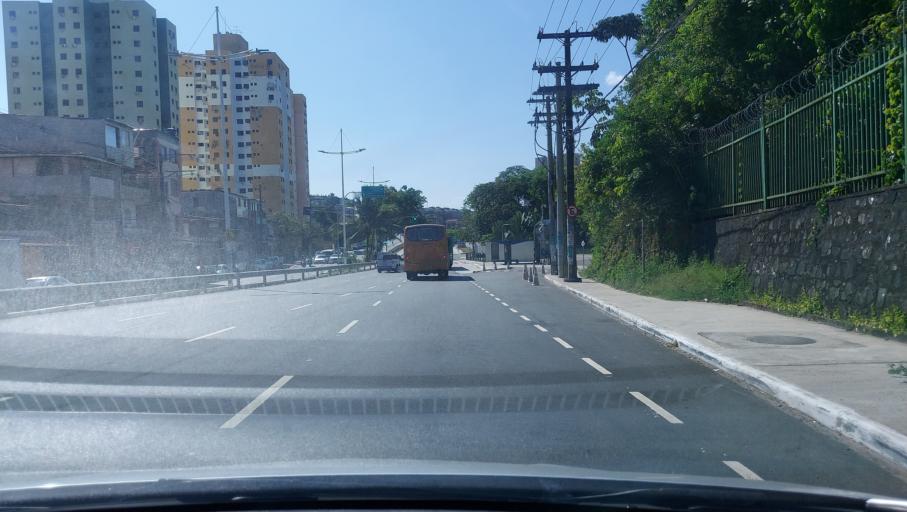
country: BR
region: Bahia
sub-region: Salvador
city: Salvador
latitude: -12.9624
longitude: -38.4369
